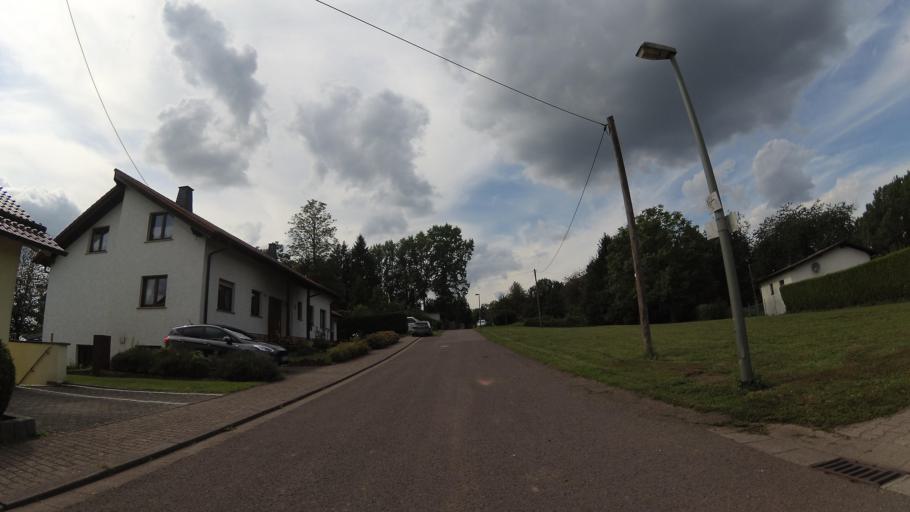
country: DE
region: Saarland
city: Illingen
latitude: 49.3760
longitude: 7.0710
